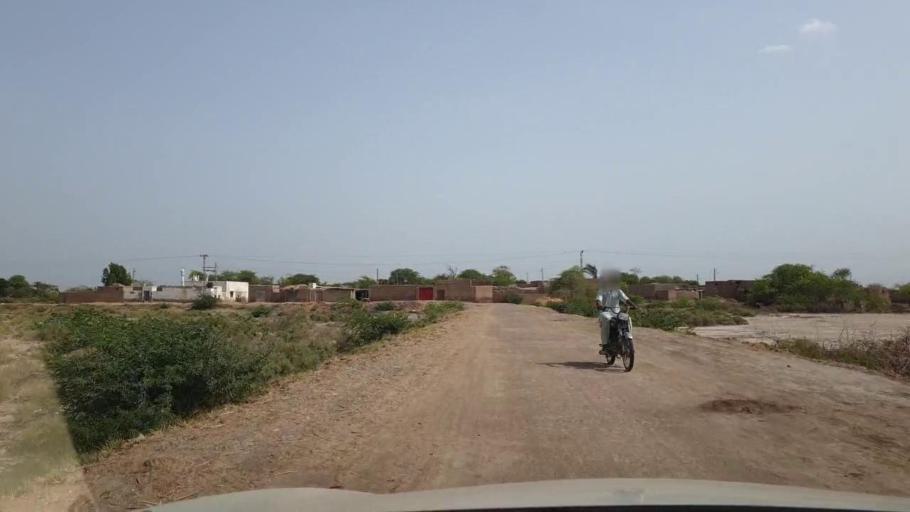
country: PK
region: Sindh
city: Mirwah Gorchani
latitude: 25.2774
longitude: 68.9583
